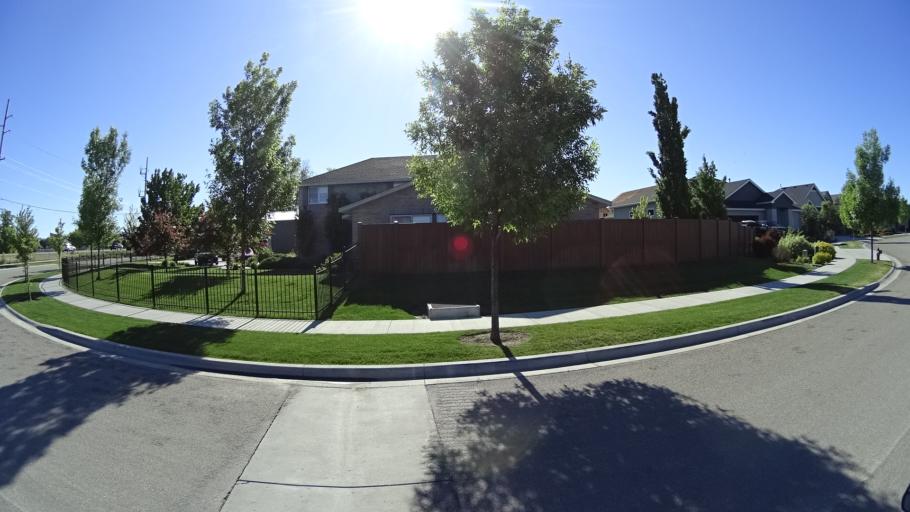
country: US
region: Idaho
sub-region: Ada County
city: Eagle
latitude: 43.6931
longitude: -116.4169
